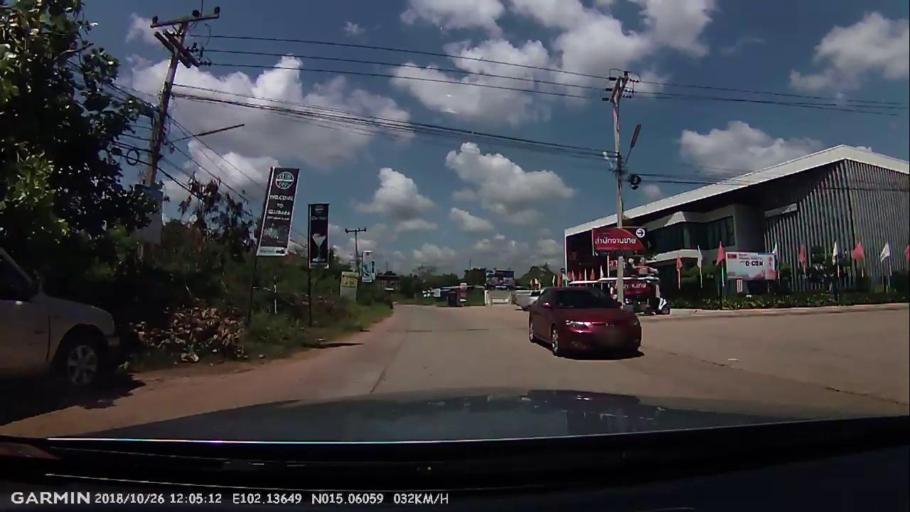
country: TH
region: Nakhon Ratchasima
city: Nakhon Ratchasima
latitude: 15.0606
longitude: 102.1364
